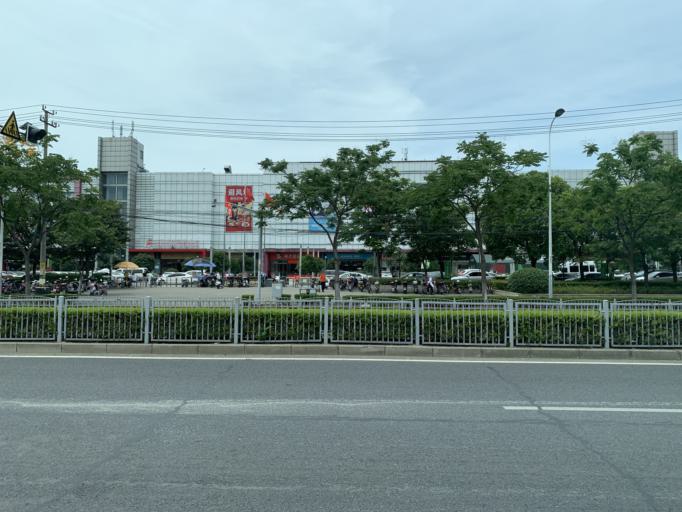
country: CN
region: Shanghai Shi
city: Kangqiao
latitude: 31.1562
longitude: 121.5607
